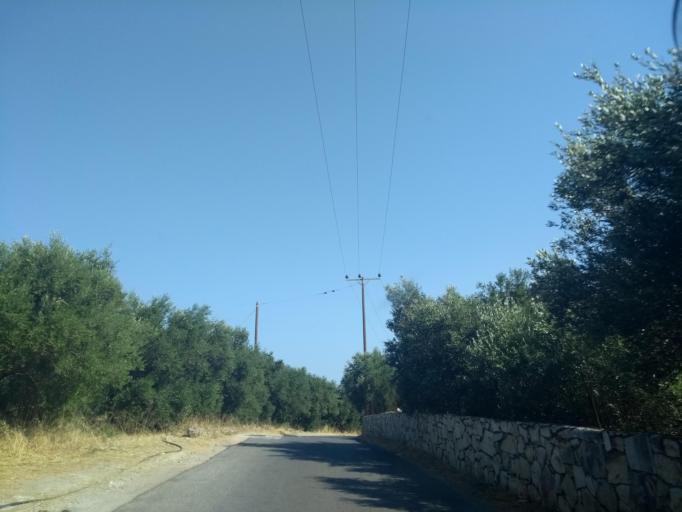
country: GR
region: Crete
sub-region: Nomos Chanias
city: Kalivai
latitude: 35.4340
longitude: 24.1754
